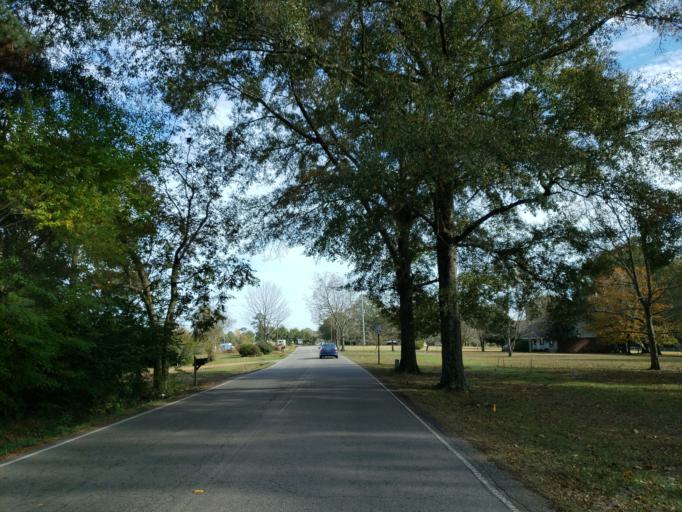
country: US
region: Mississippi
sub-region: Lamar County
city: West Hattiesburg
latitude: 31.3108
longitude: -89.3983
